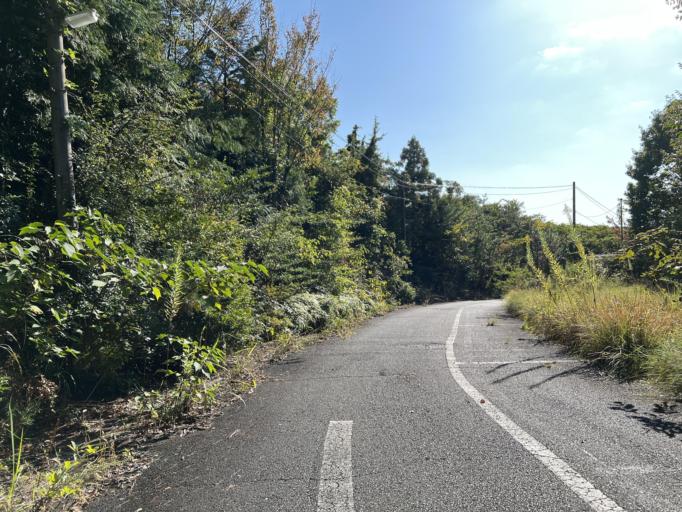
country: JP
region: Aichi
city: Okazaki
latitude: 34.9199
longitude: 137.2221
